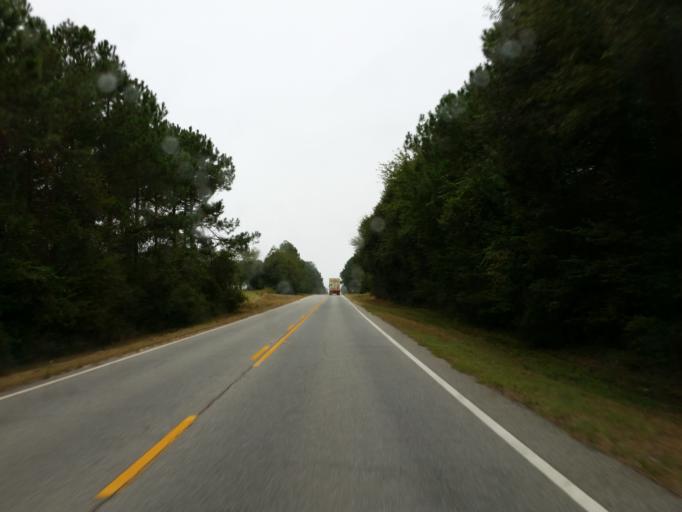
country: US
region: Georgia
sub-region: Berrien County
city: Ray City
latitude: 31.1111
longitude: -83.2961
